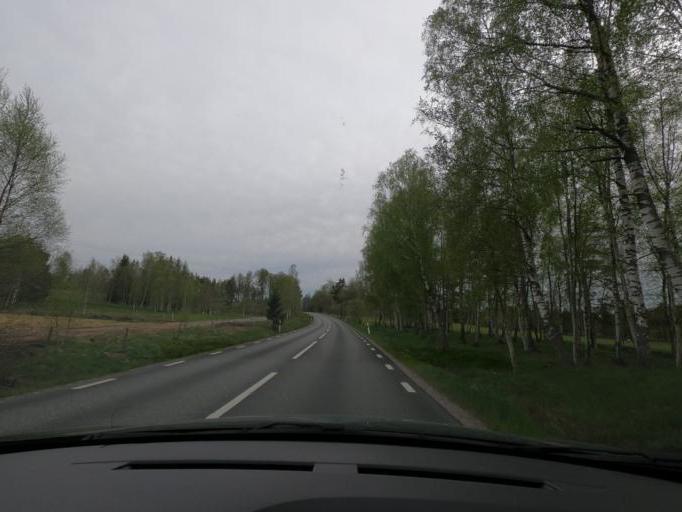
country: SE
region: Joenkoeping
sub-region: Varnamo Kommun
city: Bredaryd
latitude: 57.2120
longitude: 13.7683
